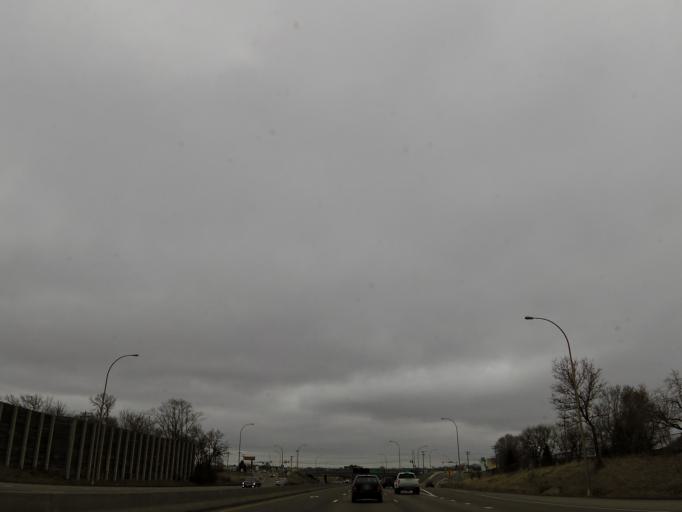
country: US
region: Minnesota
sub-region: Hennepin County
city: Bloomington
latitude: 44.8361
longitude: -93.2968
